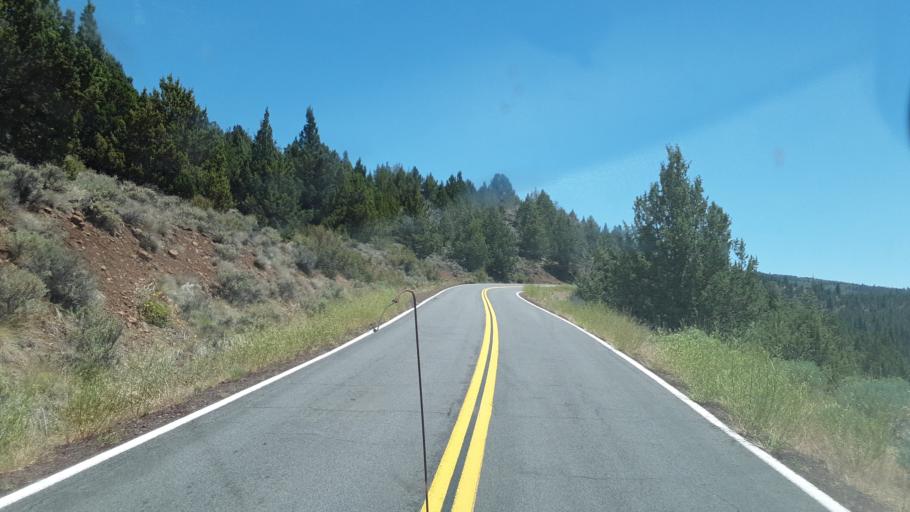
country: US
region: California
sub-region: Lassen County
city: Susanville
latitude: 40.6520
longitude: -120.6580
